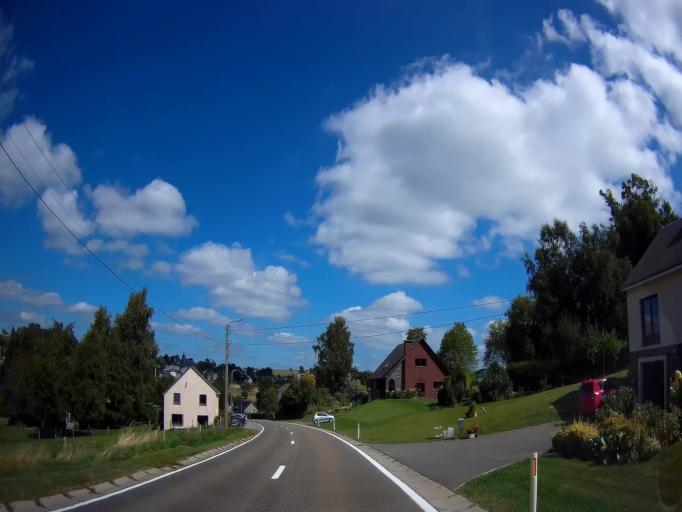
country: BE
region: Wallonia
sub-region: Province du Luxembourg
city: Bertogne
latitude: 50.0472
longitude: 5.6870
